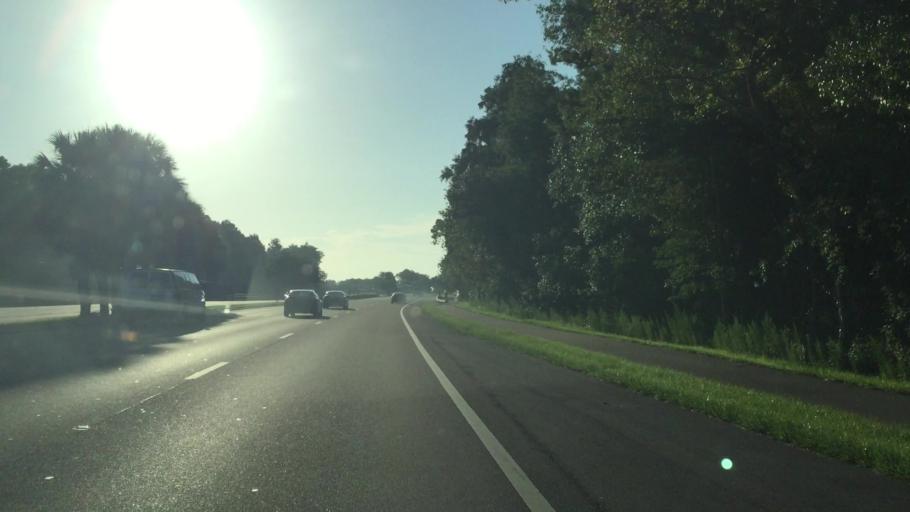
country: US
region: Florida
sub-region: Lee County
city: Villas
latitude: 26.5466
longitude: -81.8364
